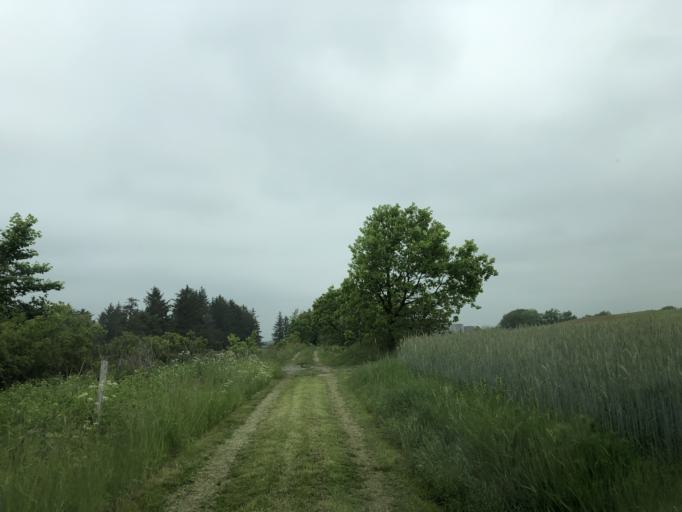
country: DK
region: Central Jutland
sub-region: Holstebro Kommune
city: Holstebro
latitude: 56.3329
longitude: 8.4806
